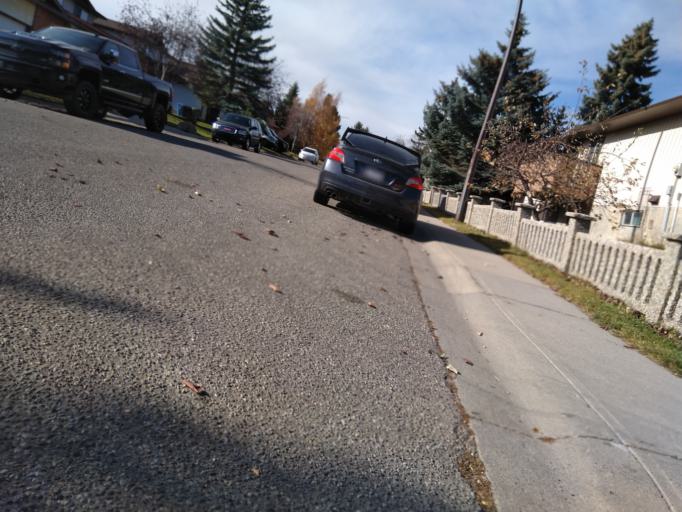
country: CA
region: Alberta
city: Calgary
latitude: 51.1255
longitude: -114.0920
